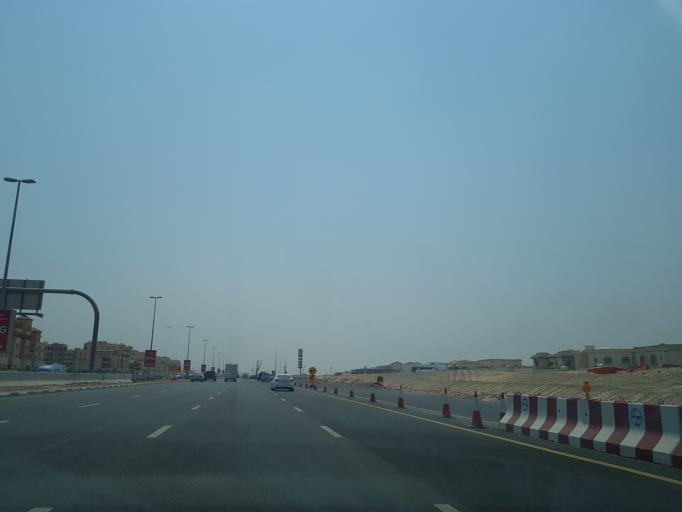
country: AE
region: Ash Shariqah
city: Sharjah
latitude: 25.2108
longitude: 55.4134
